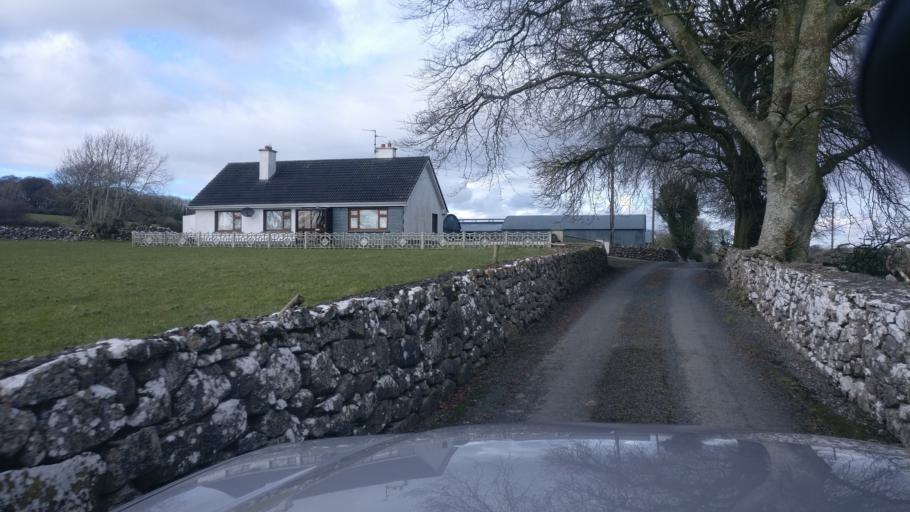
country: IE
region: Connaught
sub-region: County Galway
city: Loughrea
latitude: 53.1918
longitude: -8.4809
